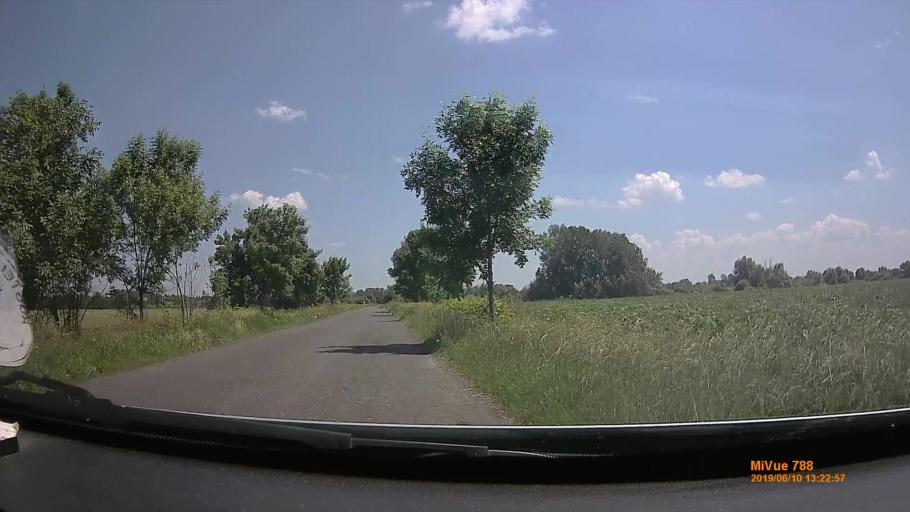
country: HU
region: Borsod-Abauj-Zemplen
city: Tiszaluc
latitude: 48.0278
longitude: 21.0881
